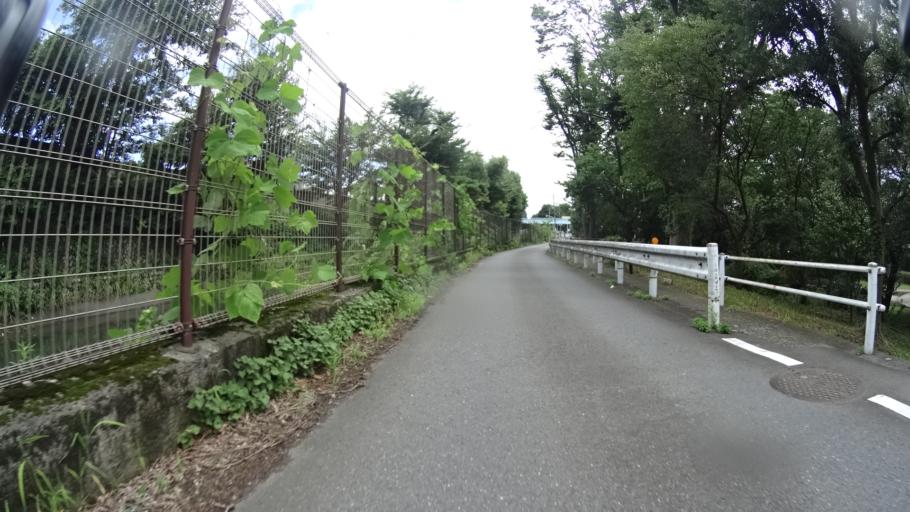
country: JP
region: Tokyo
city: Fussa
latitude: 35.7372
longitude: 139.3260
